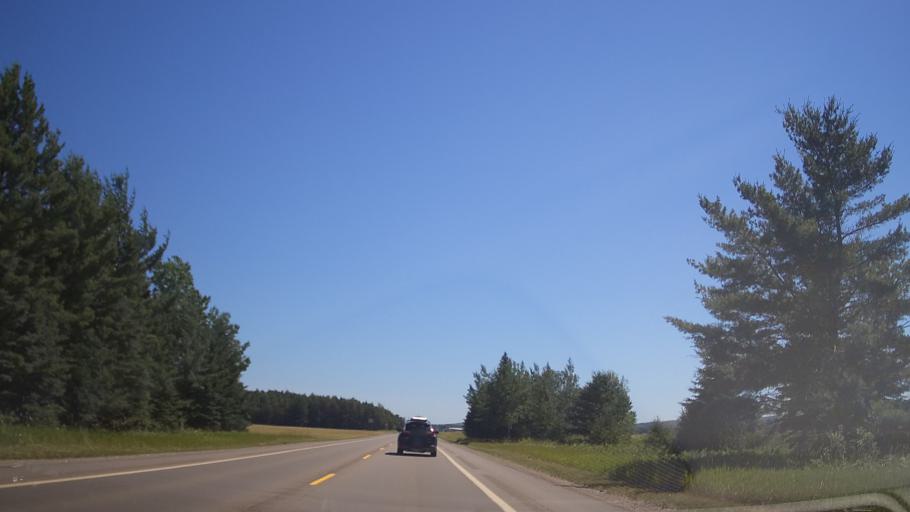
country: US
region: Michigan
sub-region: Cheboygan County
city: Indian River
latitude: 45.5839
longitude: -84.7832
